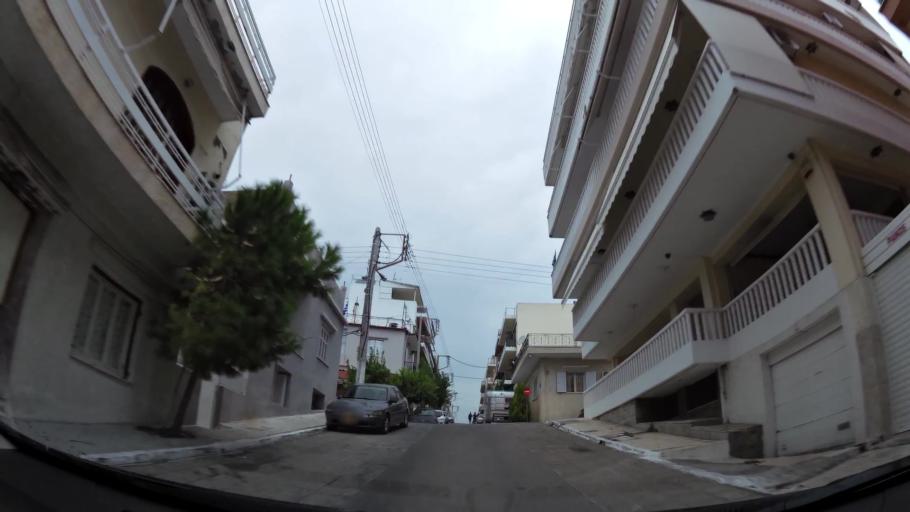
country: GR
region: Attica
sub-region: Nomarchia Athinas
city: Agia Varvara
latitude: 37.9921
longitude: 23.6546
